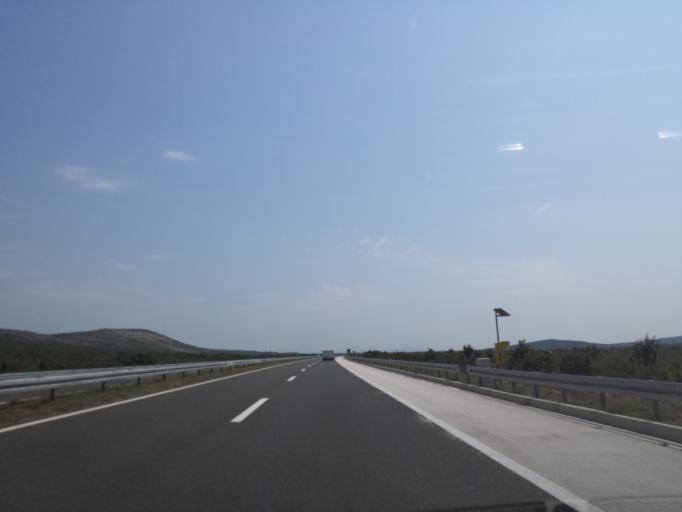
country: HR
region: Zadarska
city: Benkovac
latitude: 43.9514
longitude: 15.6845
